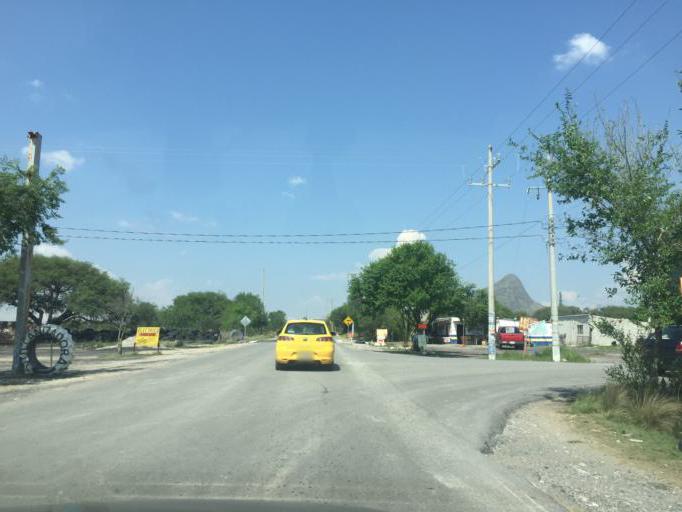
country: MX
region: Hidalgo
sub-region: Cardonal
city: Pozuelos
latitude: 20.6088
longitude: -99.0975
